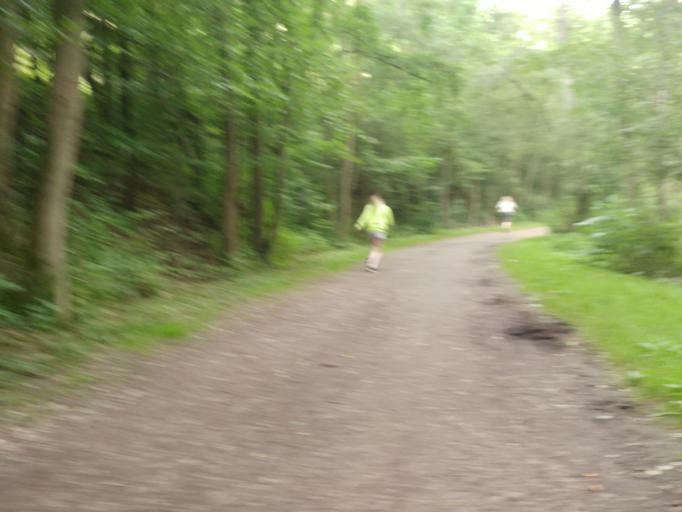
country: CZ
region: Central Bohemia
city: Roztoky
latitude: 50.1467
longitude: 14.3812
